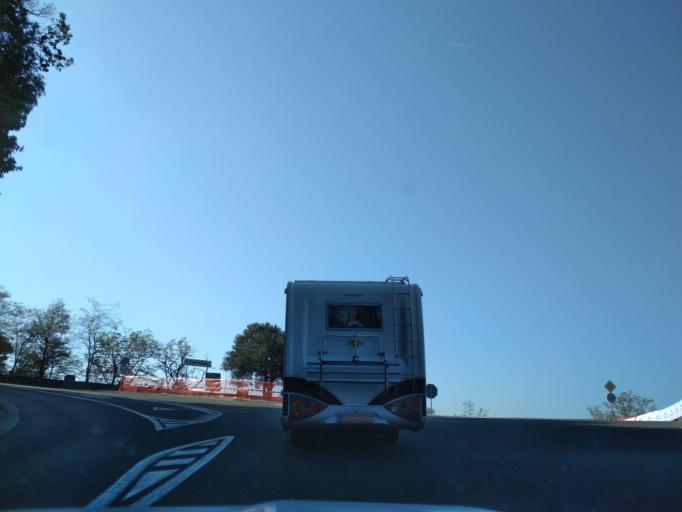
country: SM
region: San Marino
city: San Marino
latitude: 43.9392
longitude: 12.4424
